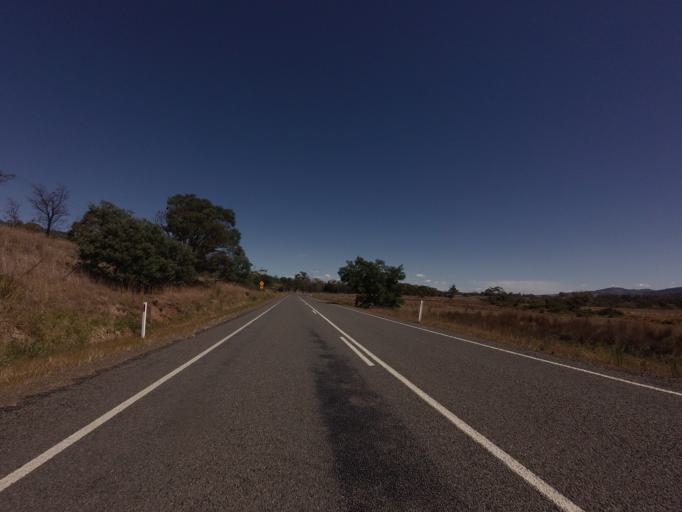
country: AU
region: Tasmania
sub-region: Northern Midlands
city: Evandale
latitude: -41.7480
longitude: 147.7819
